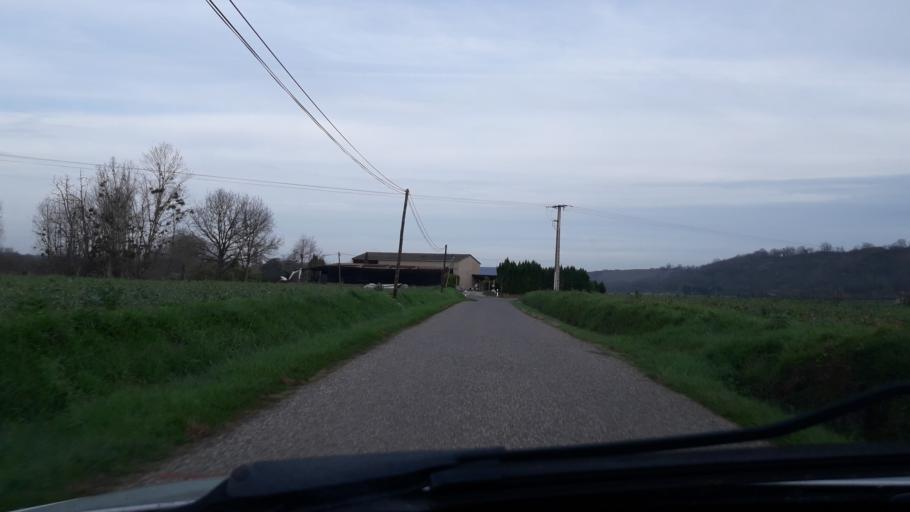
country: FR
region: Midi-Pyrenees
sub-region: Departement de la Haute-Garonne
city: Montesquieu-Volvestre
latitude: 43.1726
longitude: 1.2701
